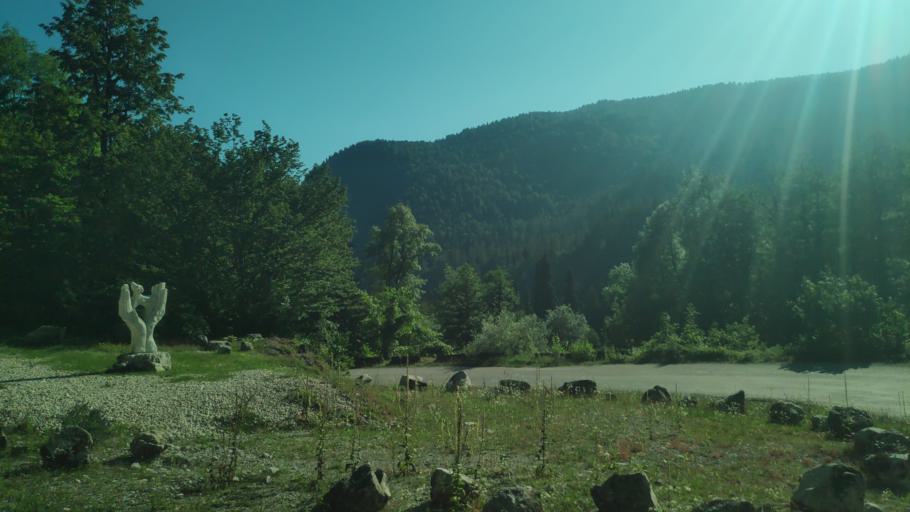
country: GE
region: Abkhazia
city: Gagra
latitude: 43.4535
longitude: 40.5454
